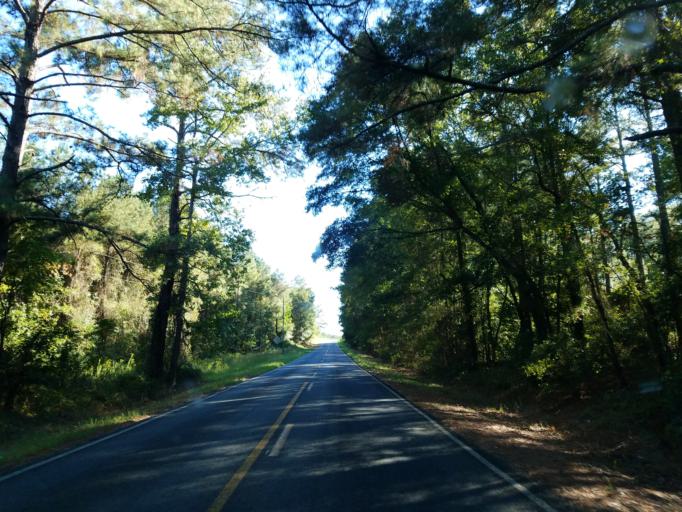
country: US
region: Georgia
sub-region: Dooly County
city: Unadilla
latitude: 32.2253
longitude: -83.8830
